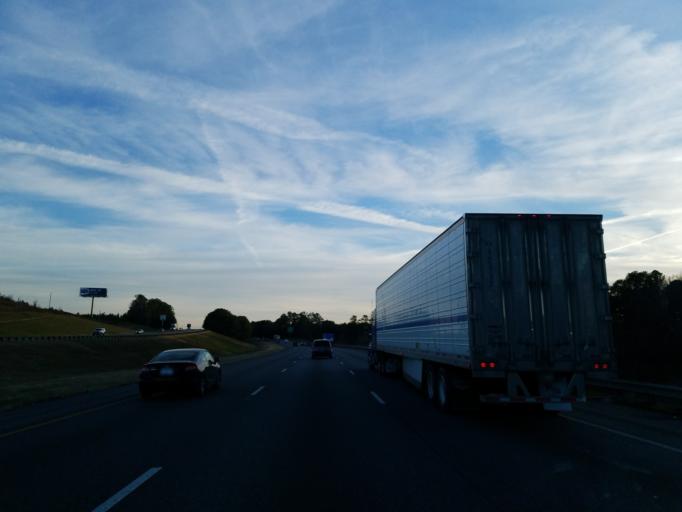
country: US
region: Georgia
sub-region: Bartow County
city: Adairsville
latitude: 34.3944
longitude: -84.9195
